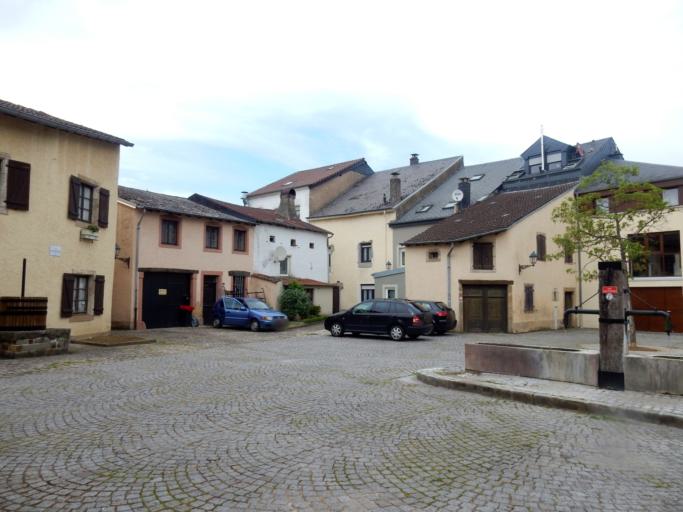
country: LU
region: Grevenmacher
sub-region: Canton de Remich
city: Bous
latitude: 49.5241
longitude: 6.3415
